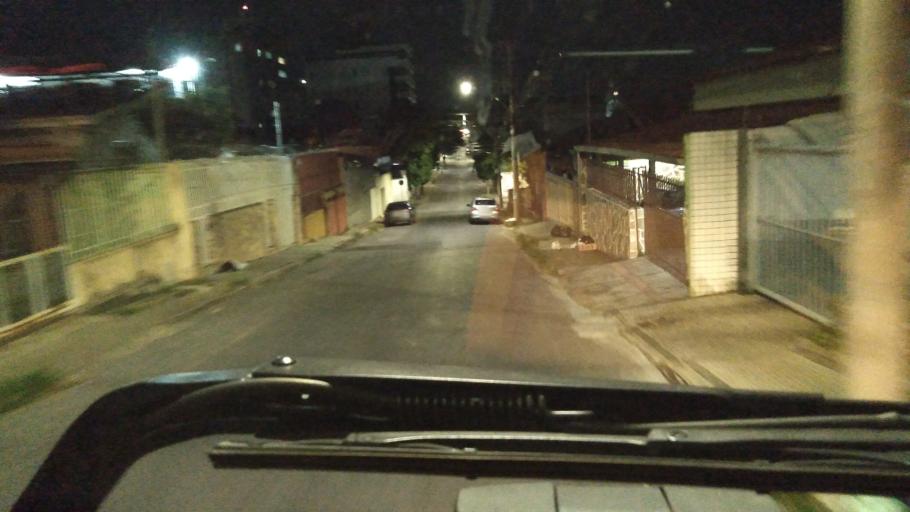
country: BR
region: Minas Gerais
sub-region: Belo Horizonte
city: Belo Horizonte
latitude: -19.9160
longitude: -43.9782
